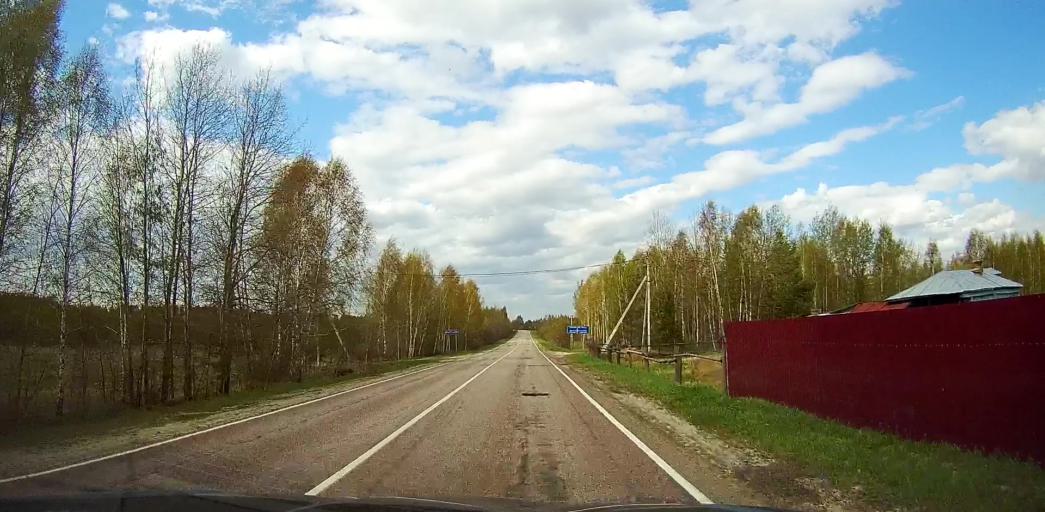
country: RU
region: Moskovskaya
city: Rakhmanovo
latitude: 55.6728
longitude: 38.6457
